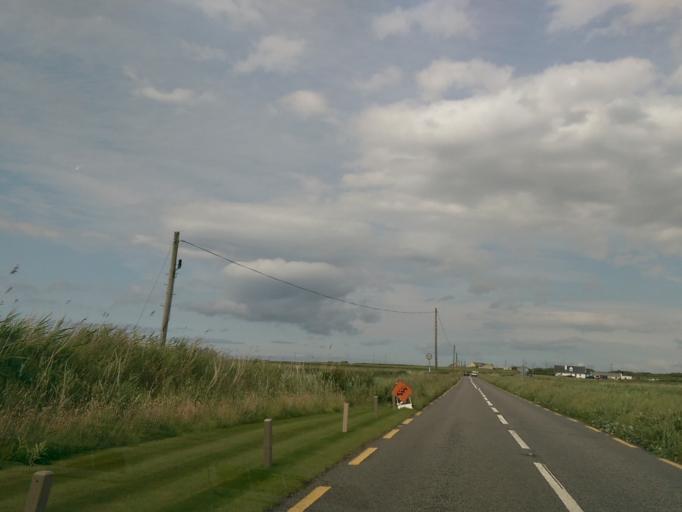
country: IE
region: Munster
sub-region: An Clar
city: Kilrush
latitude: 52.7588
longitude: -9.4763
